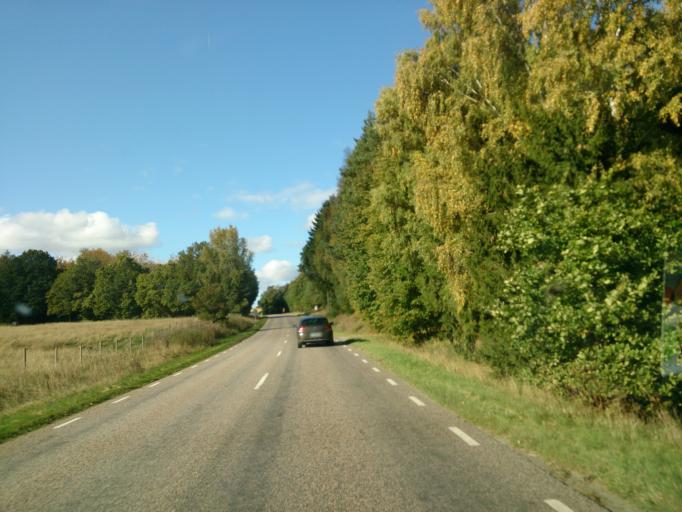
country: SE
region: Skane
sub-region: Sjobo Kommun
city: Blentarp
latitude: 55.6111
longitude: 13.5666
